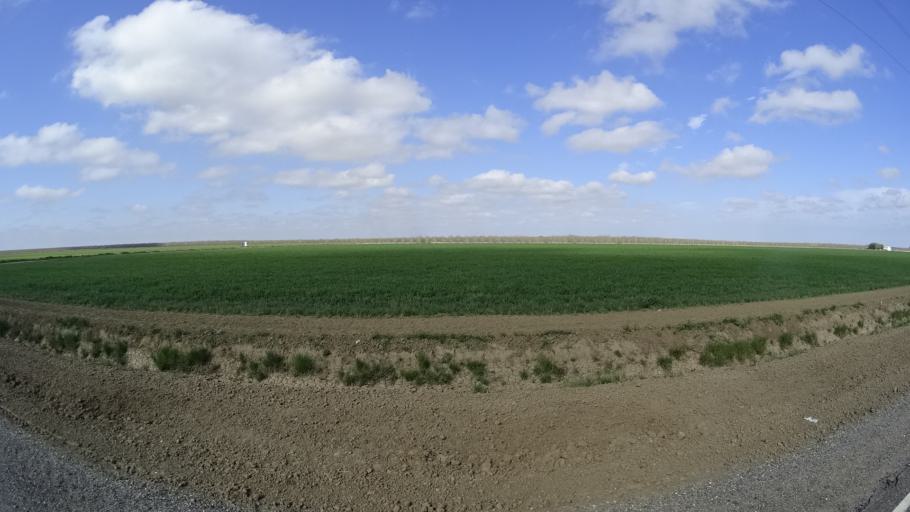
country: US
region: California
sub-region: Butte County
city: Biggs
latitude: 39.4577
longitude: -121.9303
